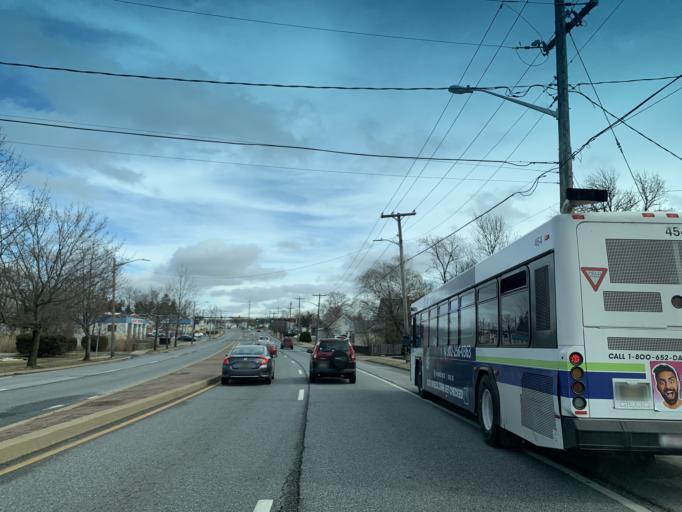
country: US
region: Delaware
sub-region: New Castle County
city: Elsmere
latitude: 39.7387
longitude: -75.5950
